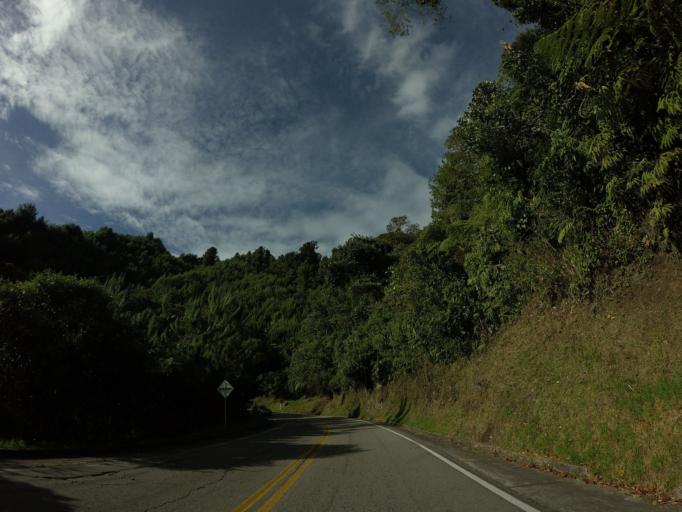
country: CO
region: Tolima
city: Herveo
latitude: 5.1382
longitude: -75.1761
